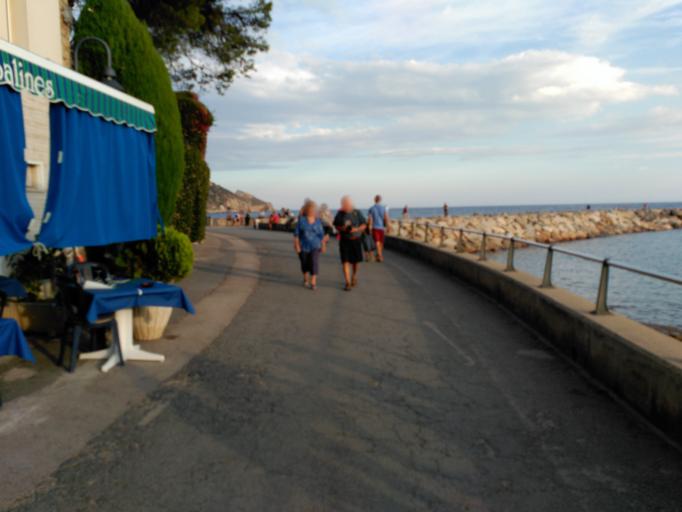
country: ES
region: Catalonia
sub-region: Provincia de Girona
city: Torroella de Montgri
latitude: 42.0534
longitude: 3.2080
